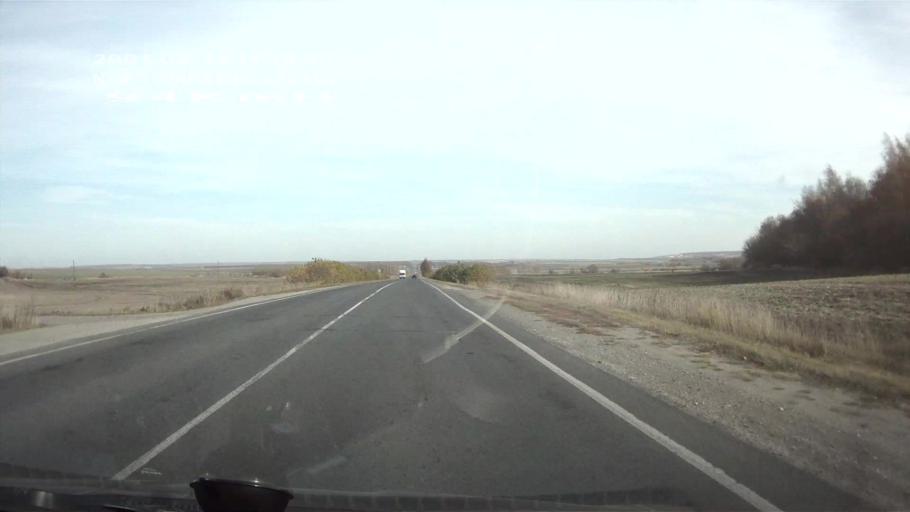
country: RU
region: Mordoviya
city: Atyashevo
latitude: 54.5378
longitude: 45.9294
